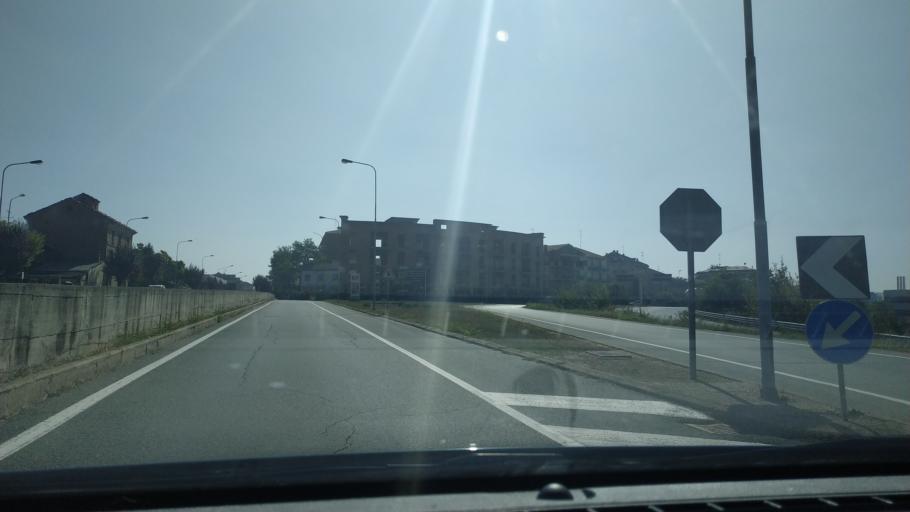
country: IT
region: Piedmont
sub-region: Provincia di Alessandria
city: Valenza
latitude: 45.0209
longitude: 8.6320
